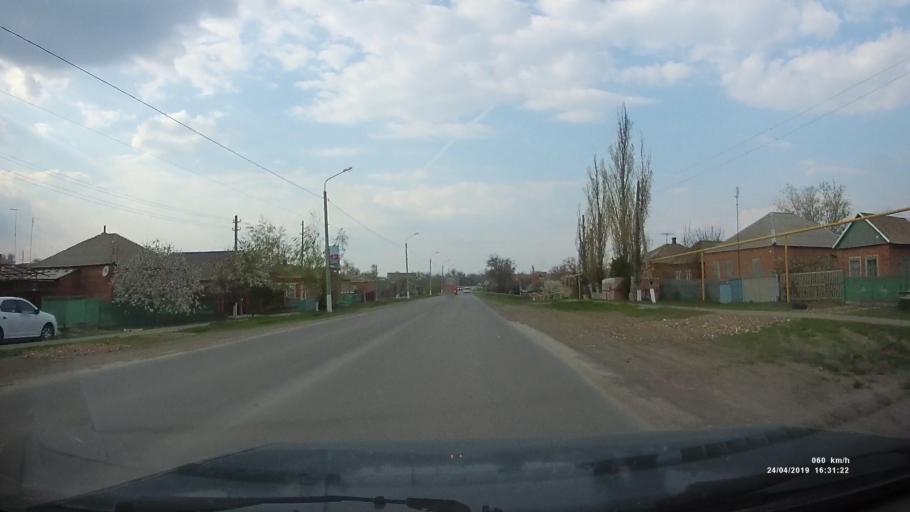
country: RU
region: Rostov
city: Orlovskiy
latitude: 46.8808
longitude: 42.0385
